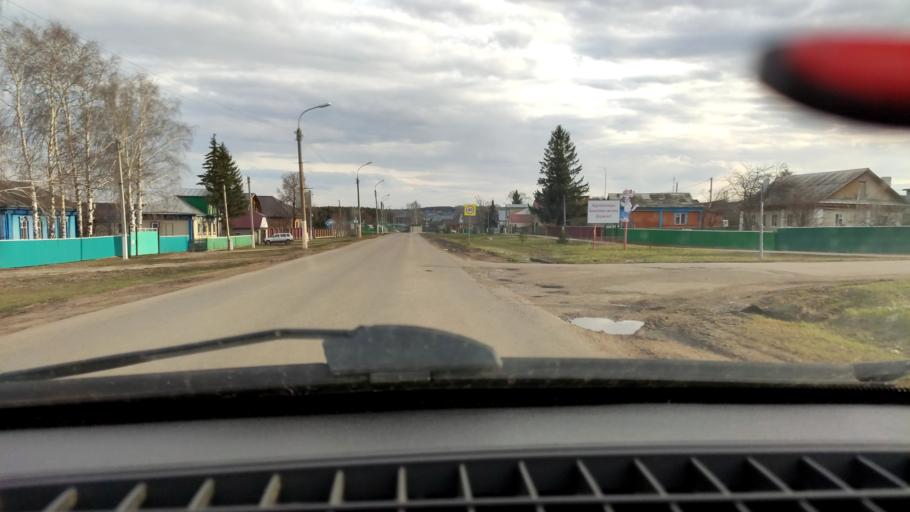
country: RU
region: Bashkortostan
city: Tolbazy
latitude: 54.0321
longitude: 55.8842
